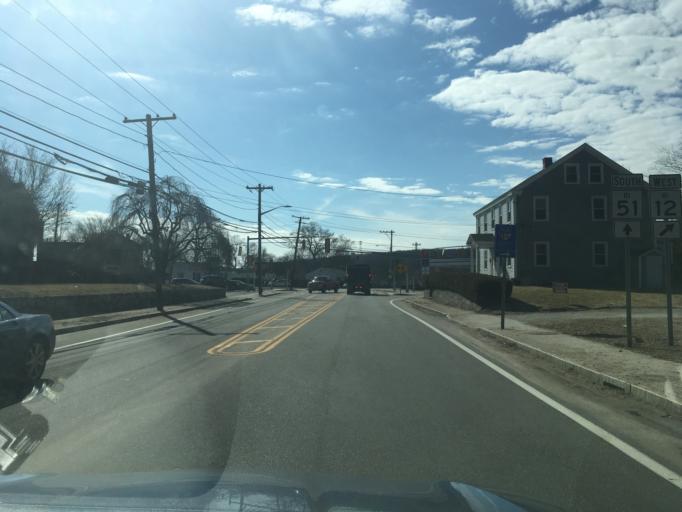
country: US
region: Rhode Island
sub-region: Providence County
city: Cranston
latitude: 41.7797
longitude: -71.4759
